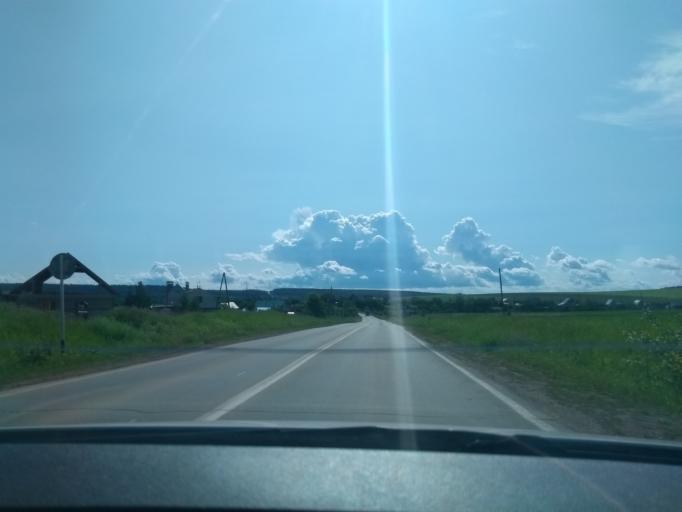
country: RU
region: Perm
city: Lobanovo
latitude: 57.8514
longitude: 56.3355
